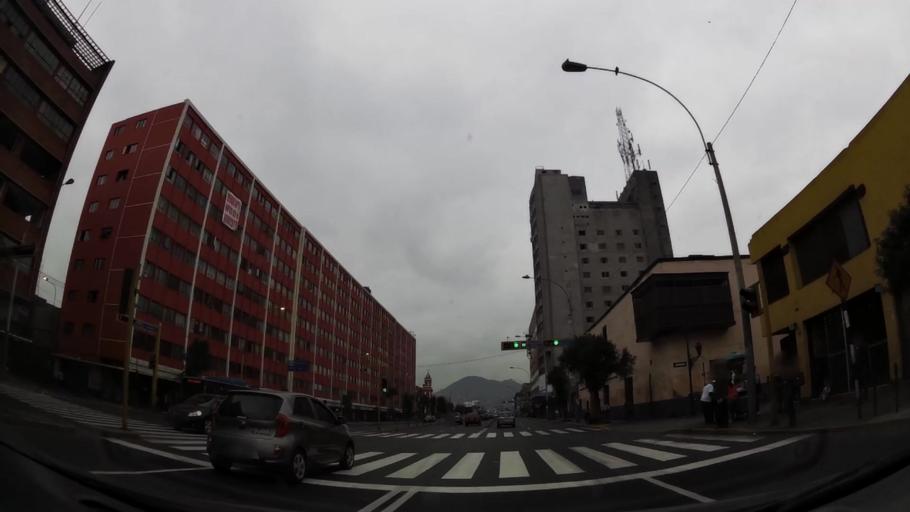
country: PE
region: Lima
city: Lima
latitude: -12.0446
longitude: -77.0362
